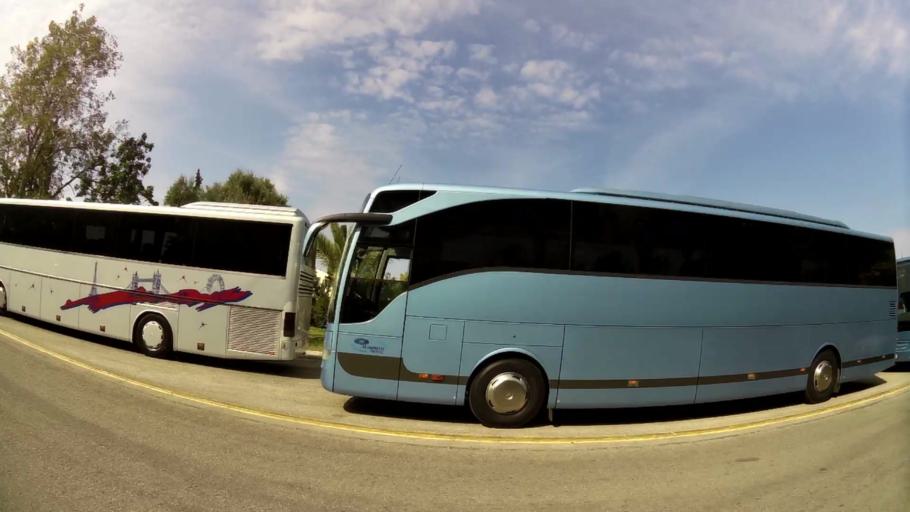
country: GR
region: Attica
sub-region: Nomarchia Athinas
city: Athens
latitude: 37.9704
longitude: 23.7155
